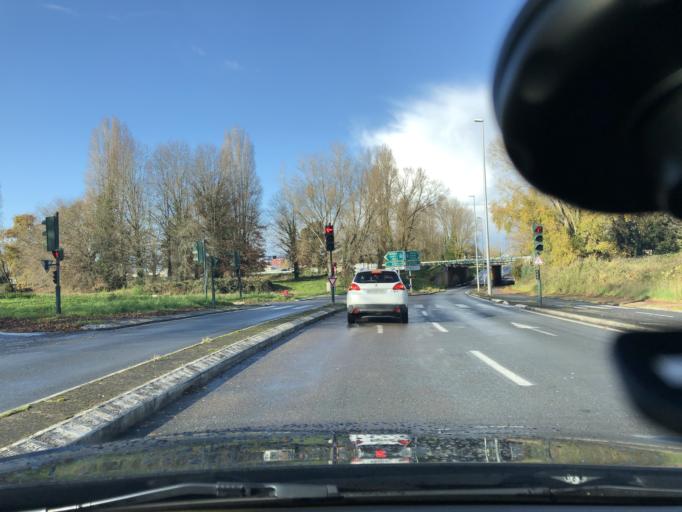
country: FR
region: Aquitaine
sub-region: Departement de la Gironde
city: Bruges
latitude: 44.8879
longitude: -0.5992
